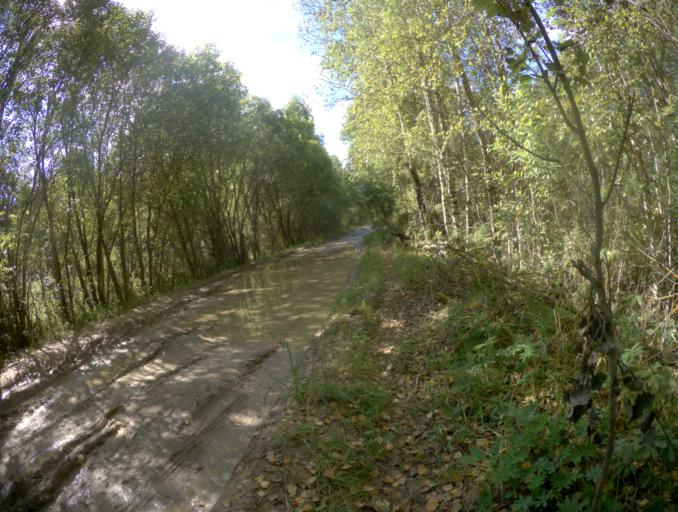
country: RU
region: Vladimir
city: Nikologory
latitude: 56.0257
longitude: 41.9428
